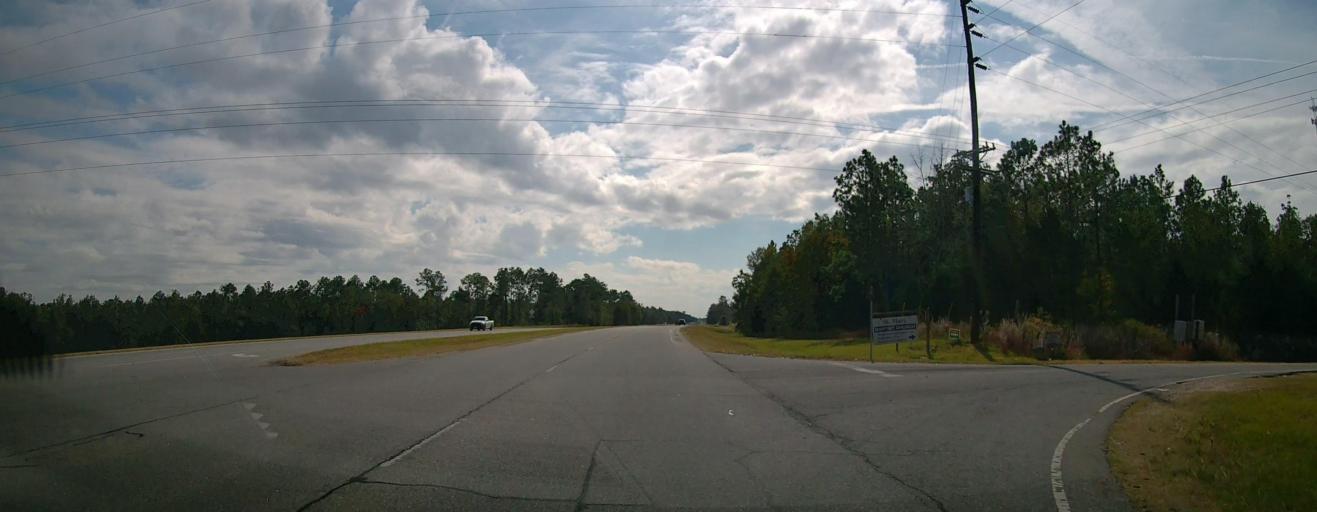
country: US
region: Georgia
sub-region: Mitchell County
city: Camilla
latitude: 31.3171
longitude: -84.1745
